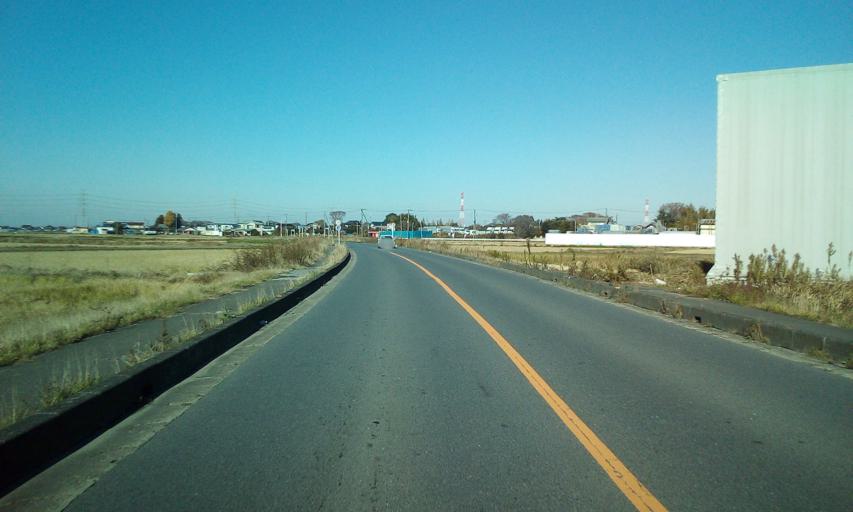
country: JP
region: Saitama
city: Yoshikawa
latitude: 35.8917
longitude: 139.8803
